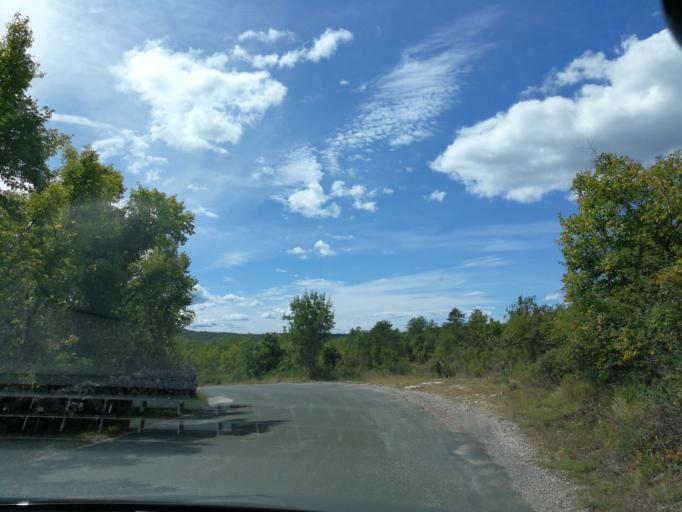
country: HR
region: Primorsko-Goranska
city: Omisalj
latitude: 45.1788
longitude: 14.5941
